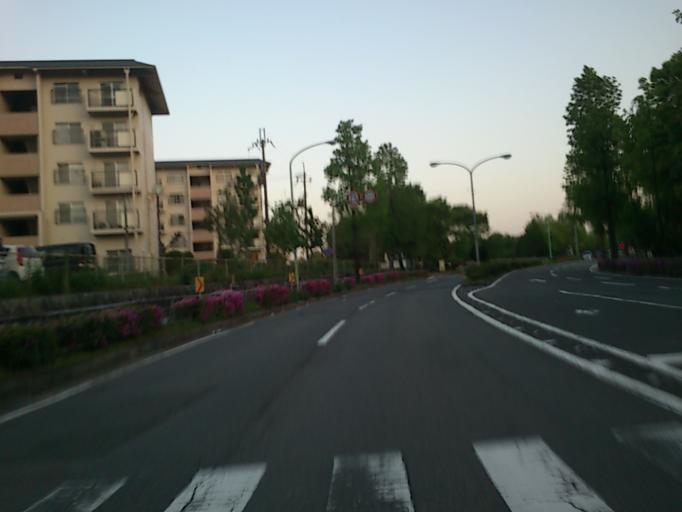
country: JP
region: Kyoto
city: Muko
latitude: 34.9594
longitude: 135.6802
